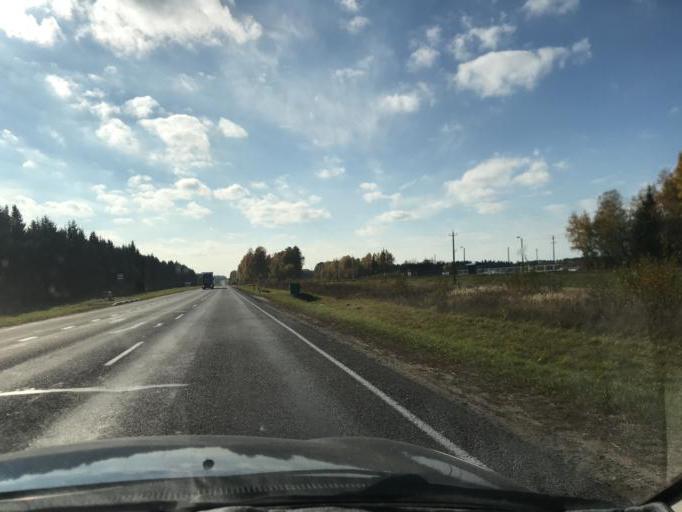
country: BY
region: Grodnenskaya
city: Voranava
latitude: 54.2101
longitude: 25.3511
